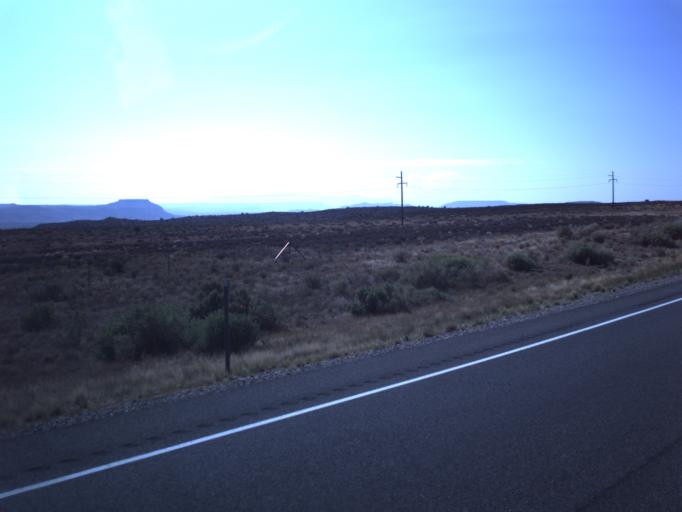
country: US
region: Utah
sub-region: San Juan County
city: Blanding
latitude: 37.3890
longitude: -109.5003
